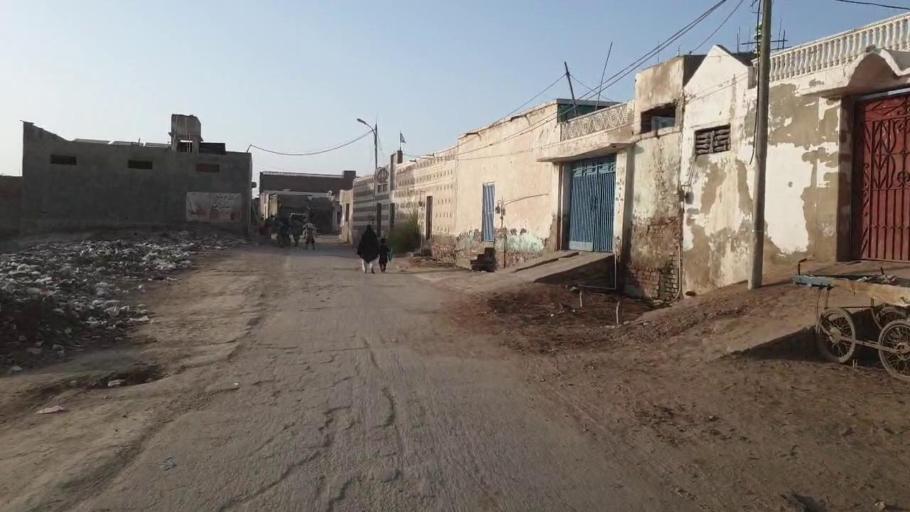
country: PK
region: Sindh
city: Jam Sahib
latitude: 26.2945
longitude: 68.6269
